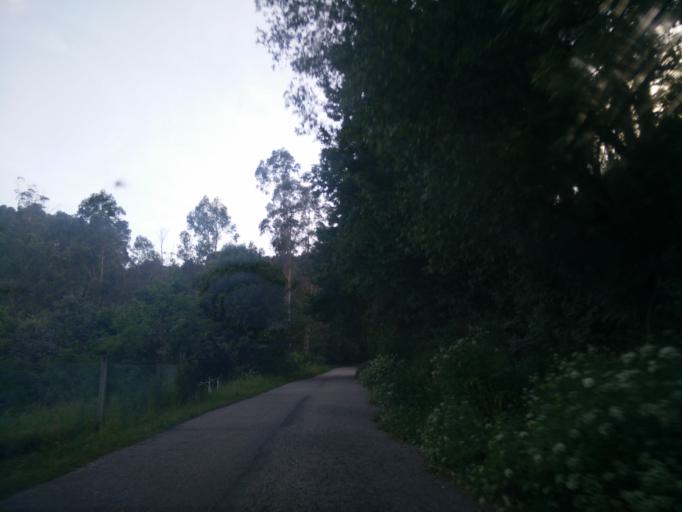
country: ES
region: Galicia
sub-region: Provincia de Pontevedra
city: Mondariz
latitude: 42.2648
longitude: -8.4086
